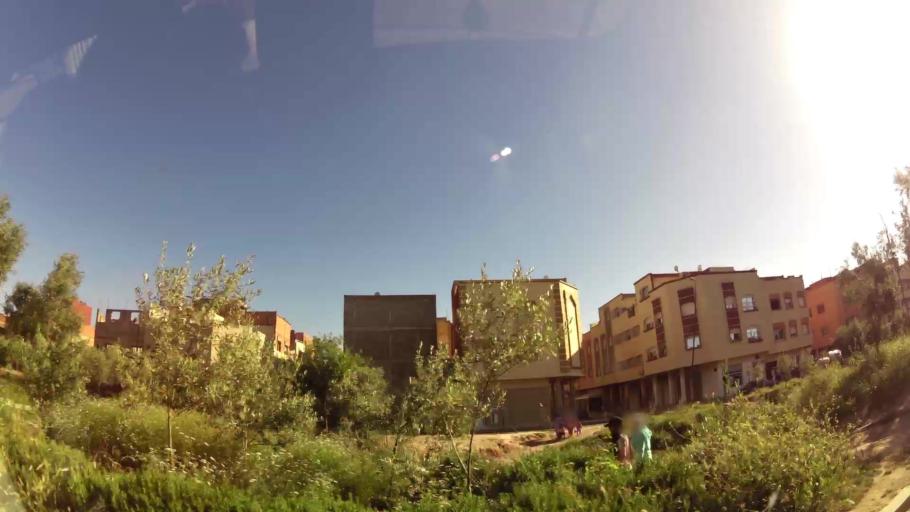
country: MA
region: Meknes-Tafilalet
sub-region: Meknes
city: Meknes
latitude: 33.8866
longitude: -5.5008
